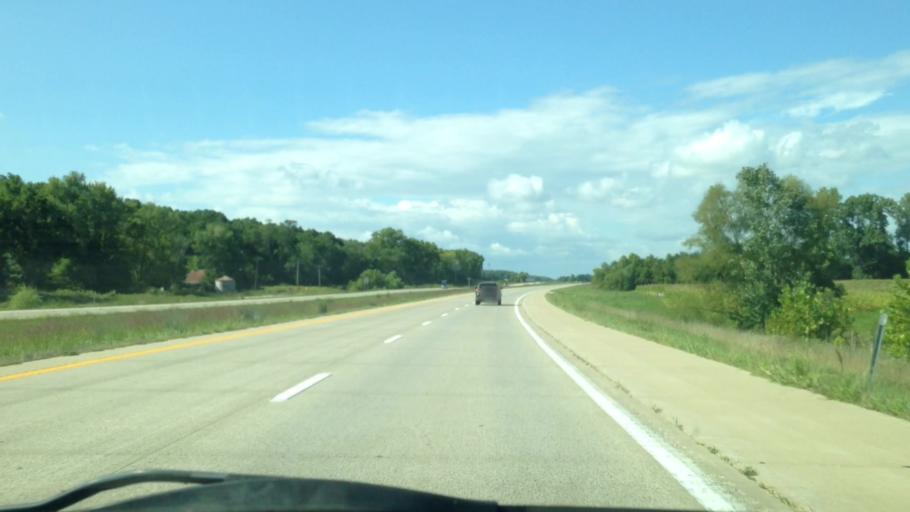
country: US
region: Illinois
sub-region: Hancock County
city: Warsaw
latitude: 40.2798
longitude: -91.5650
